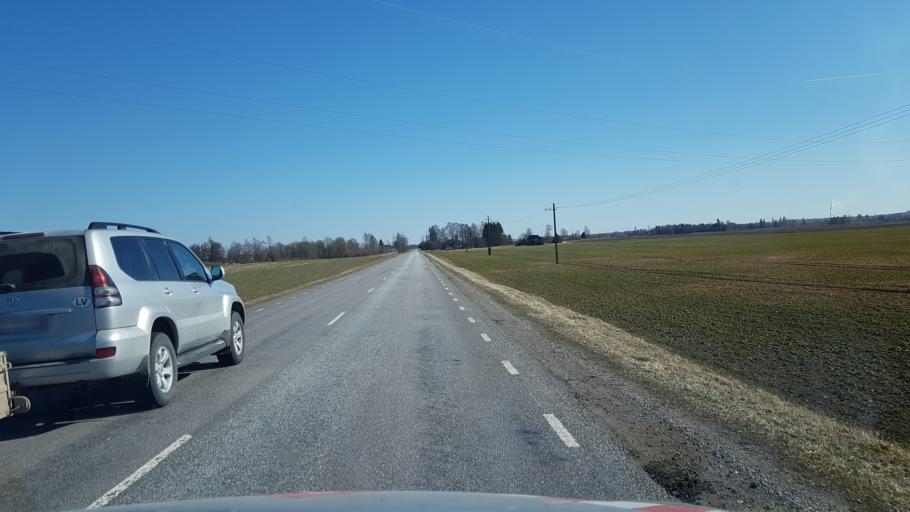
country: EE
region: Laeaene-Virumaa
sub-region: Vaeike-Maarja vald
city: Vaike-Maarja
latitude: 59.1500
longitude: 26.2235
